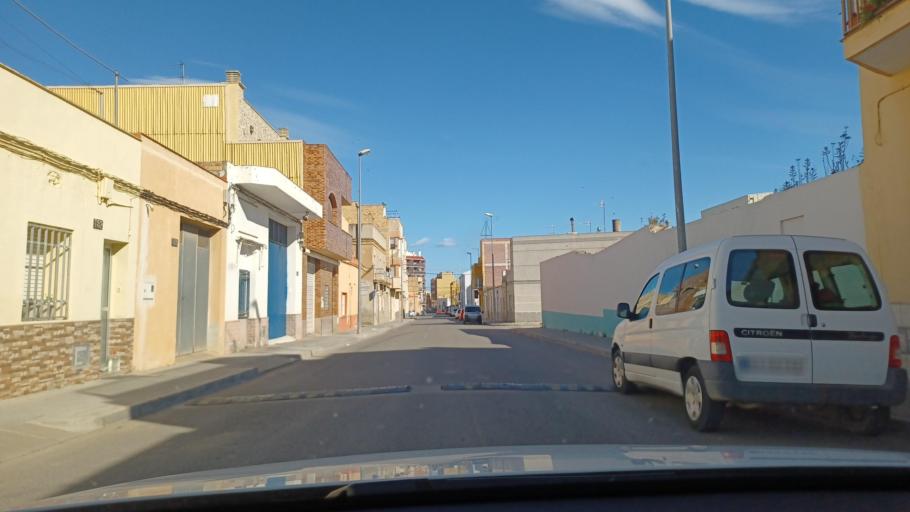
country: ES
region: Catalonia
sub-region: Provincia de Tarragona
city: Amposta
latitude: 40.7017
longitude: 0.5760
